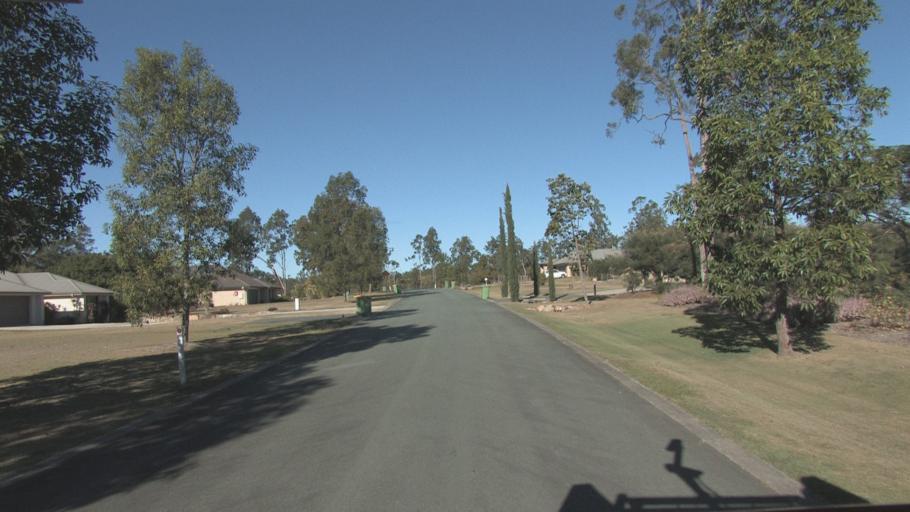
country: AU
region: Queensland
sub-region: Logan
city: North Maclean
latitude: -27.7581
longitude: 152.9664
